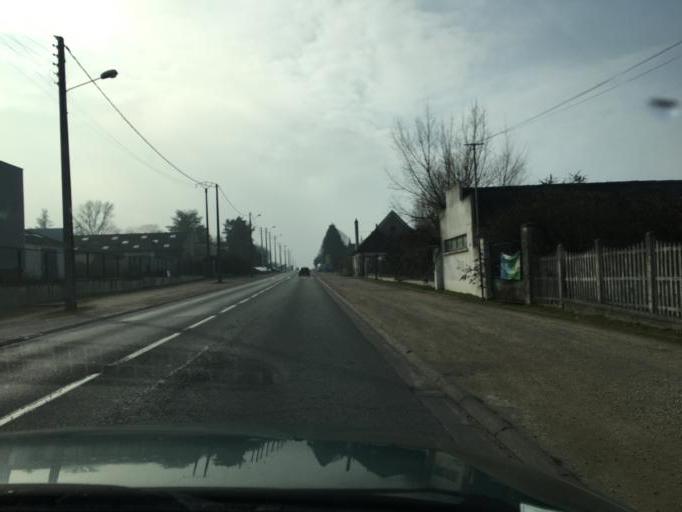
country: FR
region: Centre
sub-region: Departement du Loiret
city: Beaugency
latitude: 47.7742
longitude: 1.6223
